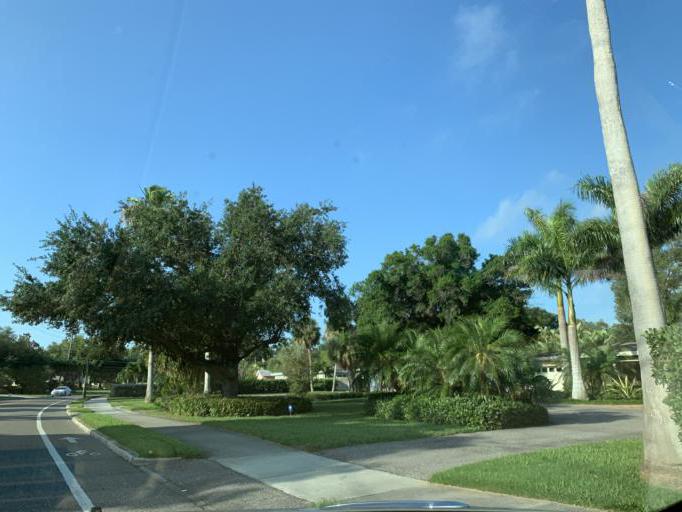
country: US
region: Florida
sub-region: Pinellas County
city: Gandy
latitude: 27.7981
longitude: -82.6104
